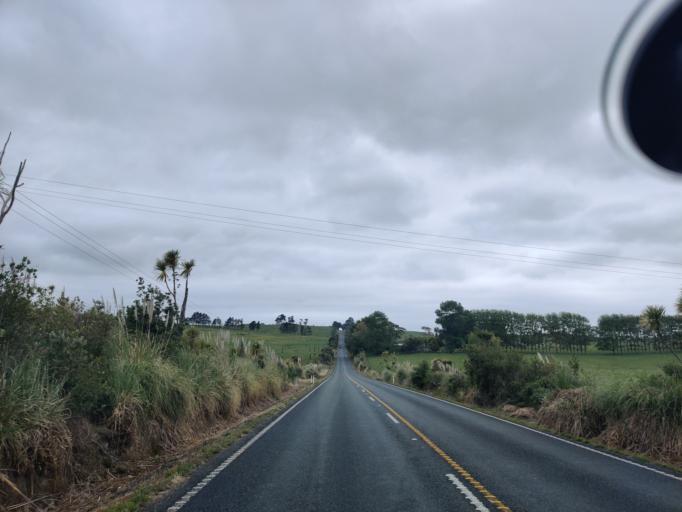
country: NZ
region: Northland
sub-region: Kaipara District
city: Dargaville
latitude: -36.1280
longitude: 174.1223
